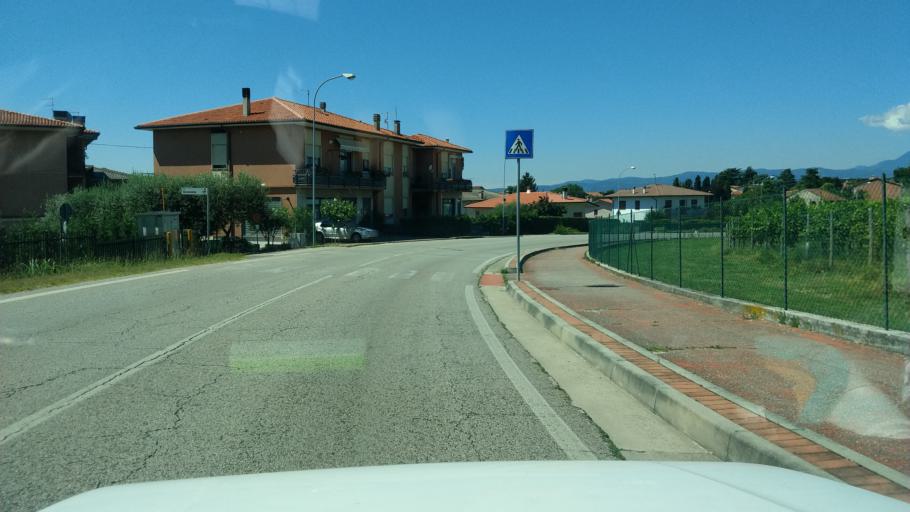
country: IT
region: Veneto
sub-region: Provincia di Vicenza
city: Breganze
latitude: 45.7068
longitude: 11.5714
